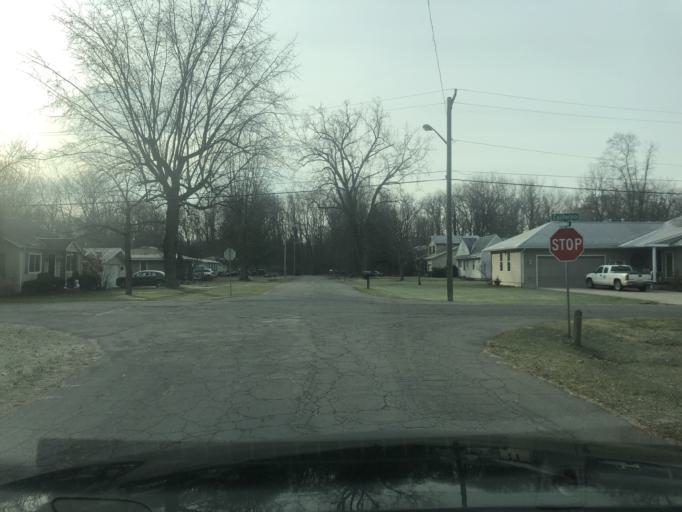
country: US
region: Michigan
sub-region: Wayne County
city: Romulus
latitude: 42.1860
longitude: -83.3281
